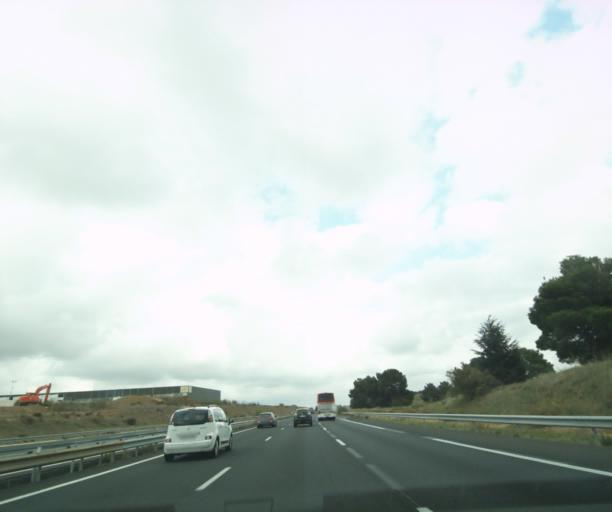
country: FR
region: Languedoc-Roussillon
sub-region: Departement de l'Herault
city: Cers
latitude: 43.3356
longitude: 3.2874
